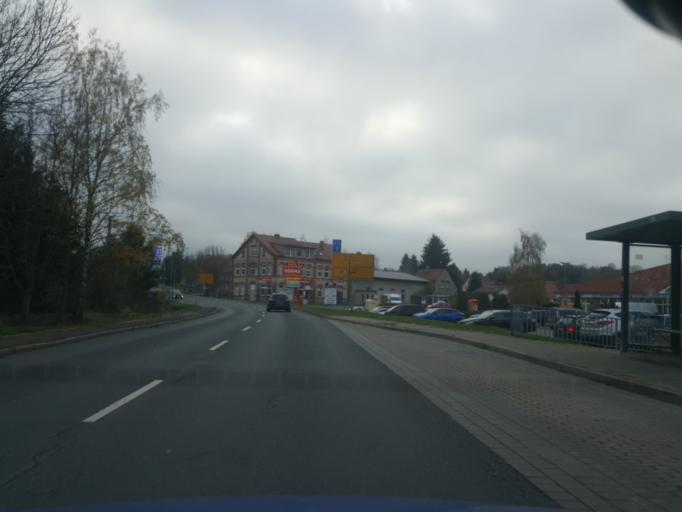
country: DE
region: Saxony-Anhalt
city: Wimmelburg
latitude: 51.5204
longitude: 11.5130
